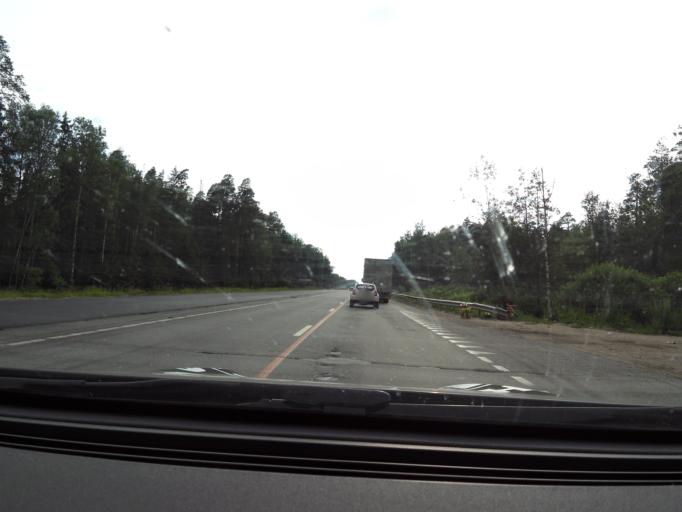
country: RU
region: Vladimir
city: Stepantsevo
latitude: 56.2327
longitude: 41.7872
